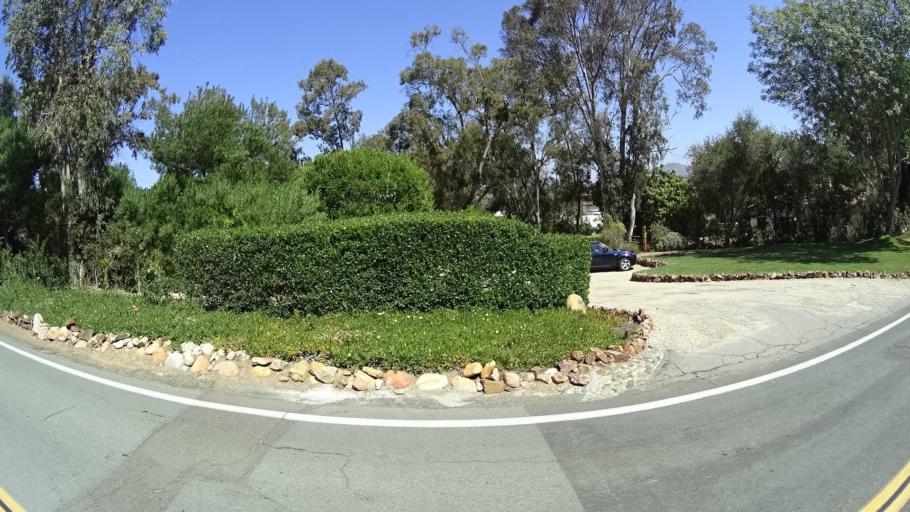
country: US
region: California
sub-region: San Diego County
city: Rancho Santa Fe
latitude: 33.0186
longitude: -117.2086
